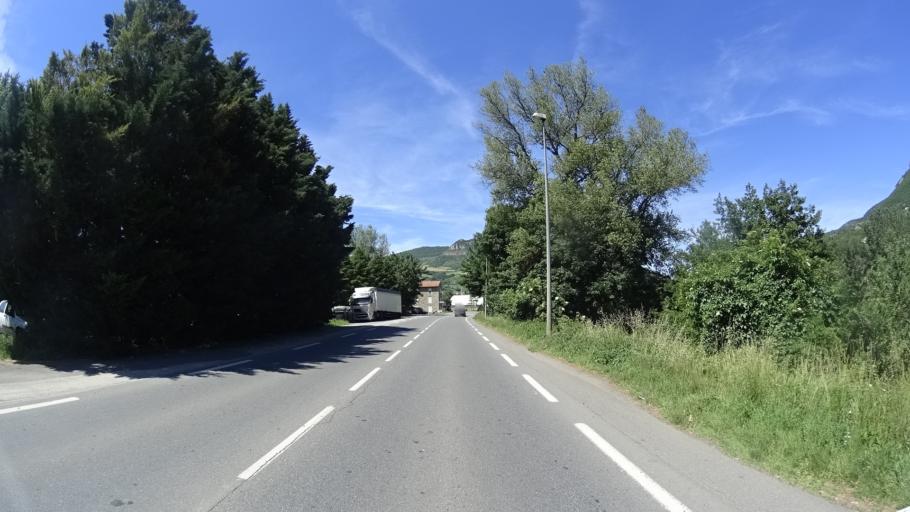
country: FR
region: Midi-Pyrenees
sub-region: Departement de l'Aveyron
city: Millau
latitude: 44.1046
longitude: 3.0845
